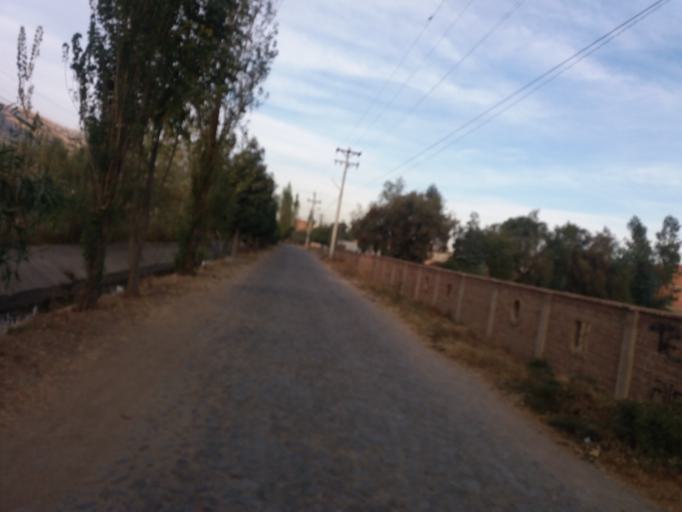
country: BO
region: Cochabamba
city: Cochabamba
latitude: -17.3569
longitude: -66.1964
